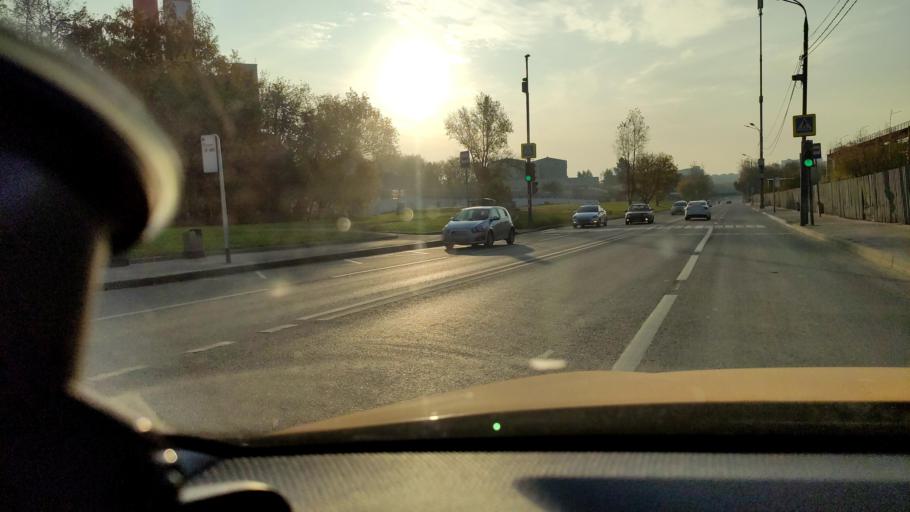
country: RU
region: Moscow
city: Metrogorodok
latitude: 55.8212
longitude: 37.7631
